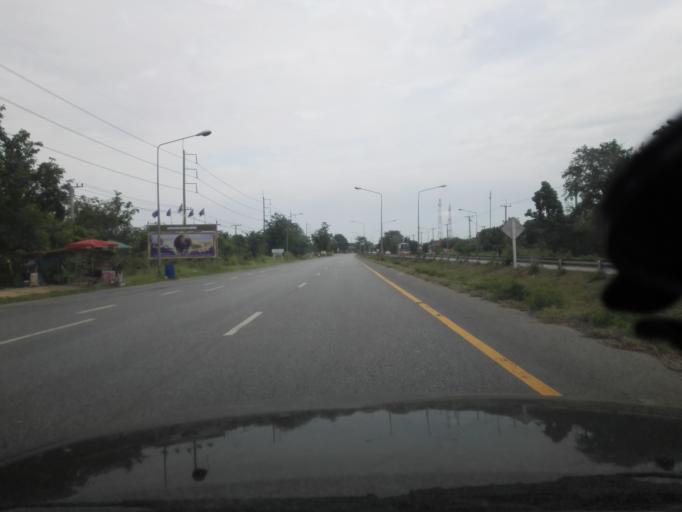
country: TH
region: Kamphaeng Phet
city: Khlong Khlung
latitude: 16.0988
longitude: 99.7211
